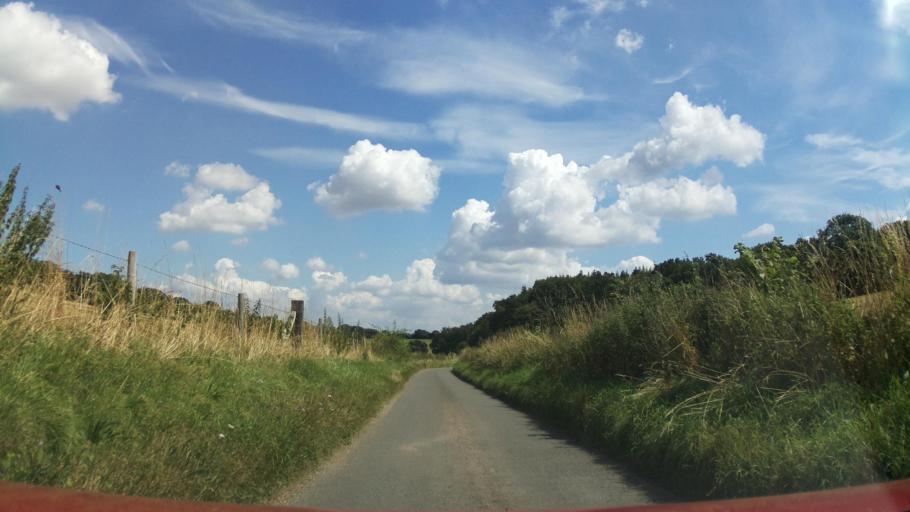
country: GB
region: England
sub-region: West Berkshire
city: Farnborough
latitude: 51.5117
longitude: -1.3726
